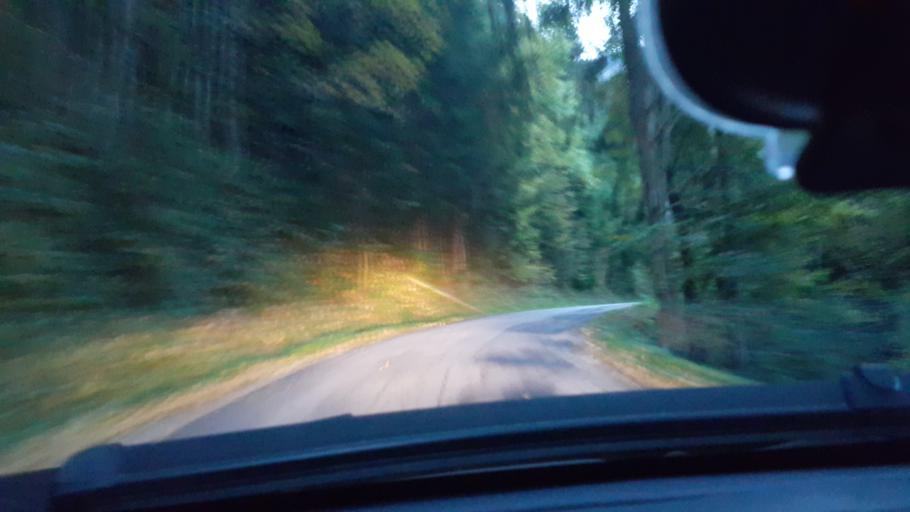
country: SI
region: Vitanje
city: Vitanje
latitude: 46.4073
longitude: 15.2922
